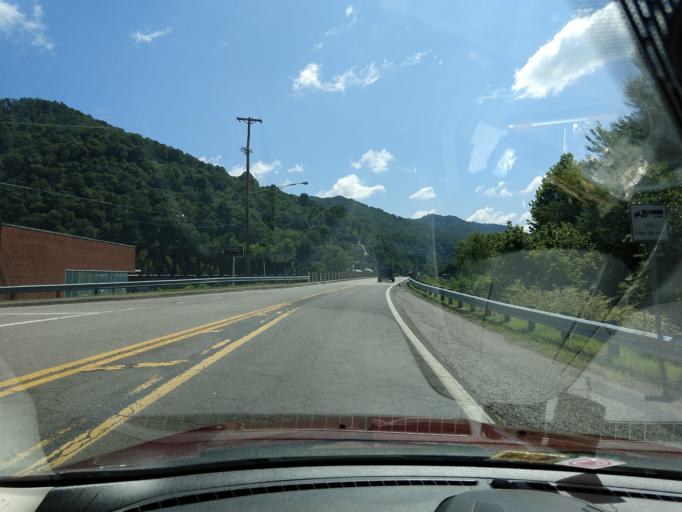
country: US
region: West Virginia
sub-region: Fayette County
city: Ansted
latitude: 38.1635
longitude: -81.1976
